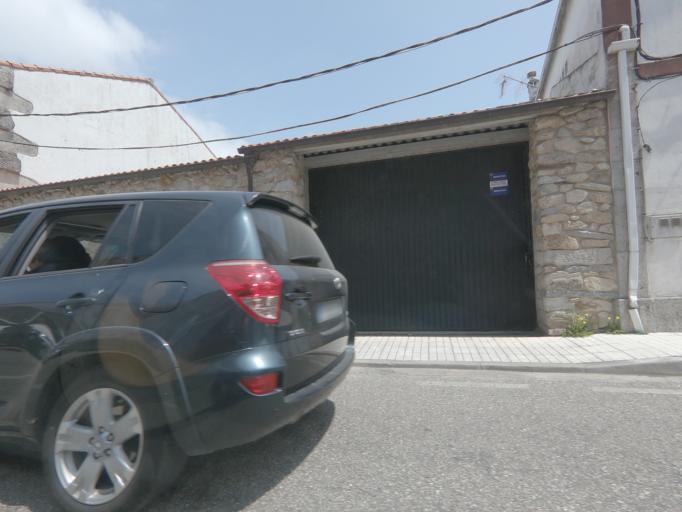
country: ES
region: Galicia
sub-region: Provincia de Pontevedra
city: A Guarda
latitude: 41.8906
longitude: -8.8533
